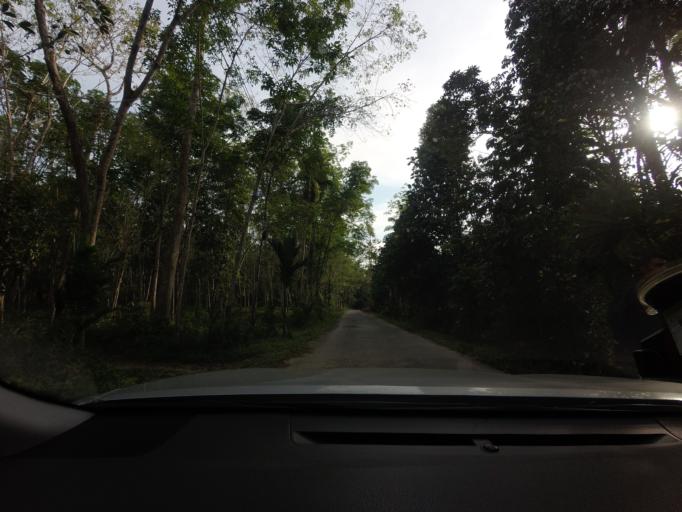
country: TH
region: Narathiwat
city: Ra-ngae
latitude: 6.3058
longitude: 101.7762
